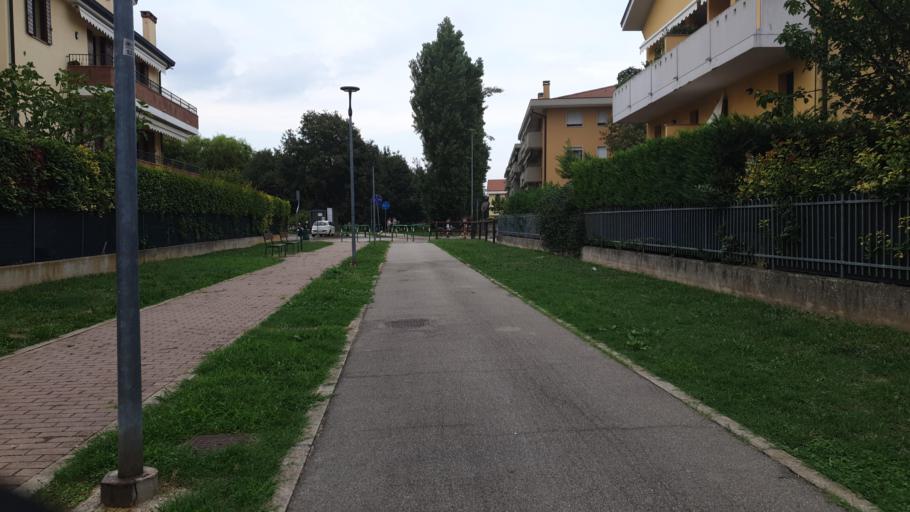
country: IT
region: Veneto
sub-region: Provincia di Padova
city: Mandriola-Sant'Agostino
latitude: 45.3474
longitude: 11.8591
